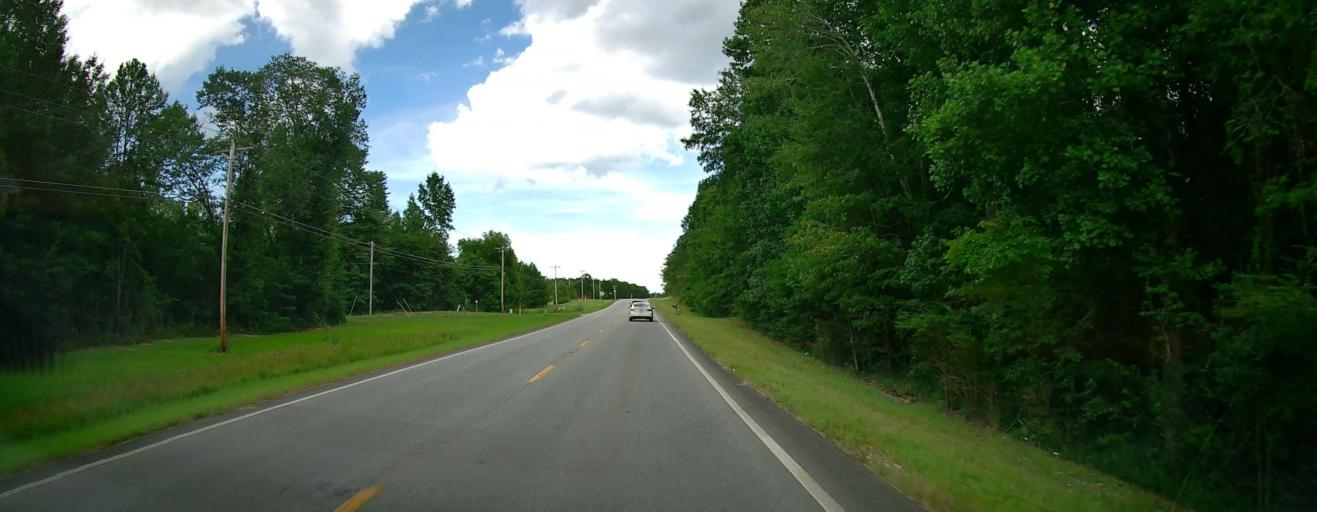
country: US
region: Alabama
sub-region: Russell County
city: Ladonia
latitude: 32.4450
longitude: -85.2733
